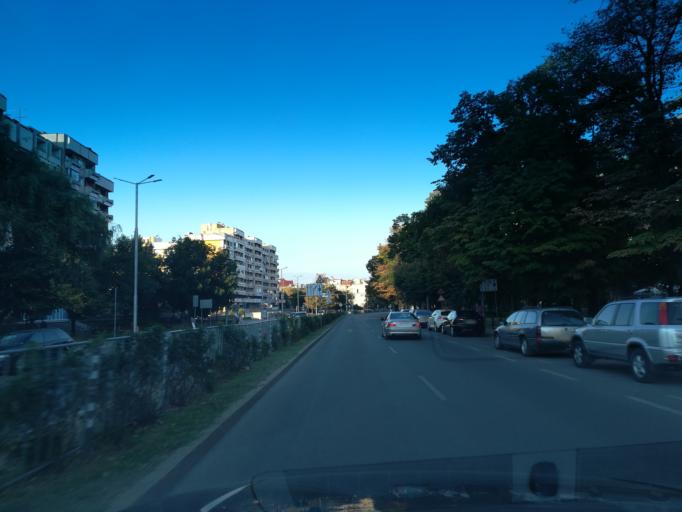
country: BG
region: Plovdiv
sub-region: Obshtina Plovdiv
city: Plovdiv
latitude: 42.1455
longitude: 24.7568
